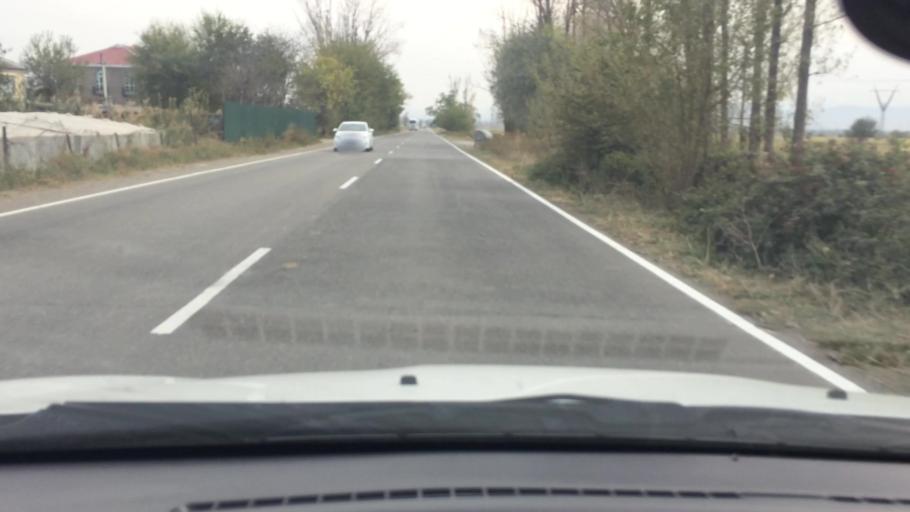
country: GE
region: Kvemo Kartli
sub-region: Gardabani
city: Gardabani
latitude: 41.4462
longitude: 44.9966
